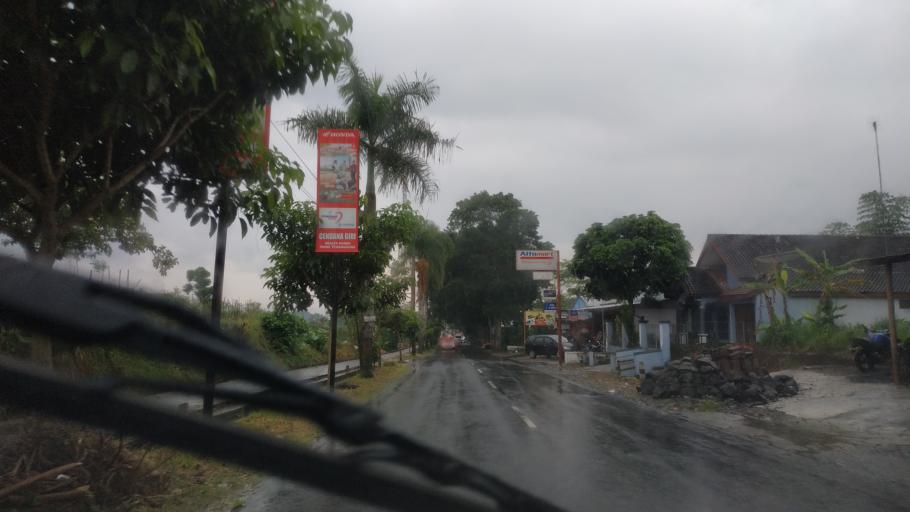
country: ID
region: Central Java
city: Magelang
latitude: -7.3145
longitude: 110.1667
